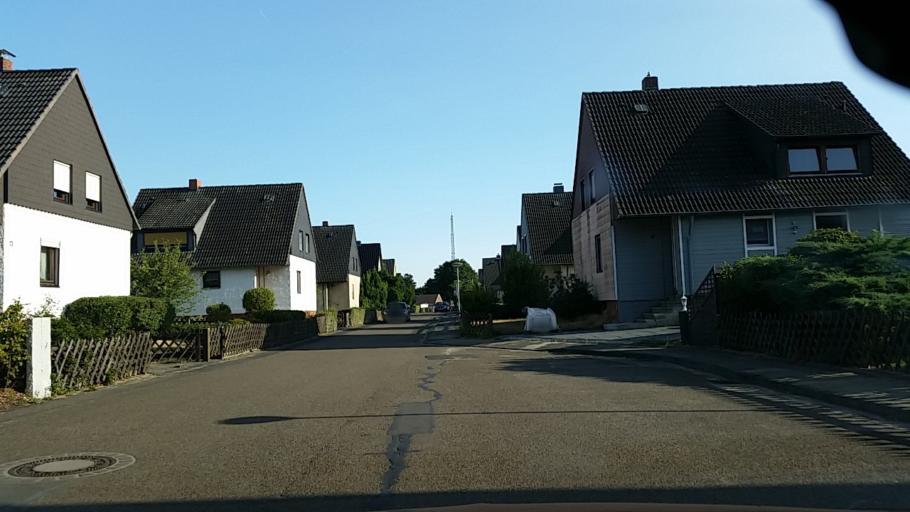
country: DE
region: Lower Saxony
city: Lehre
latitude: 52.3299
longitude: 10.6747
